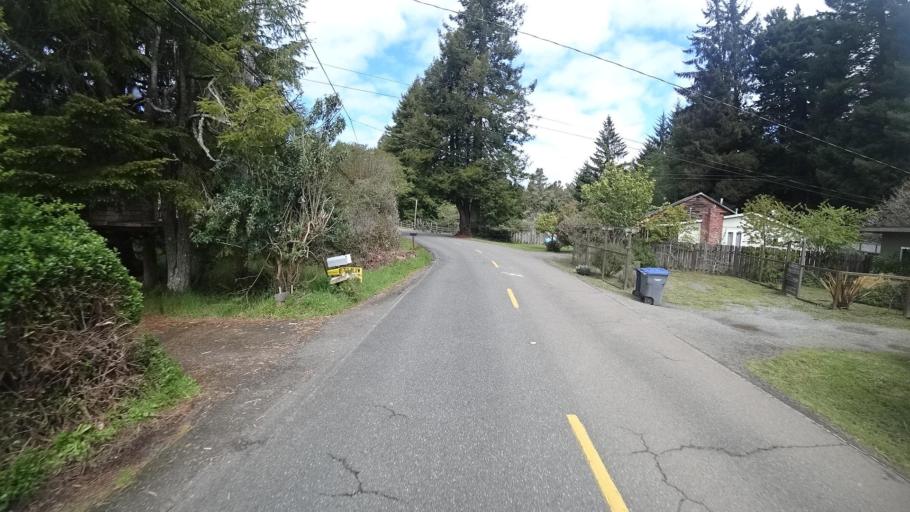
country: US
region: California
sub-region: Humboldt County
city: Bayside
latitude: 40.8620
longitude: -124.0408
